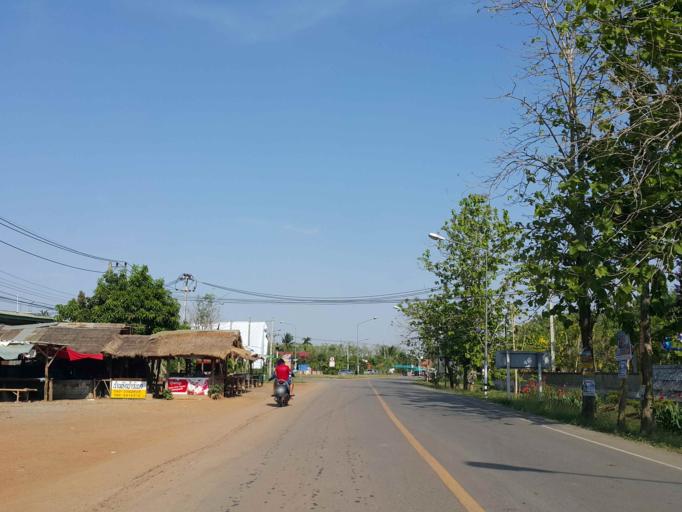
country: TH
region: Sukhothai
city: Thung Saliam
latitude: 17.3270
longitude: 99.6289
